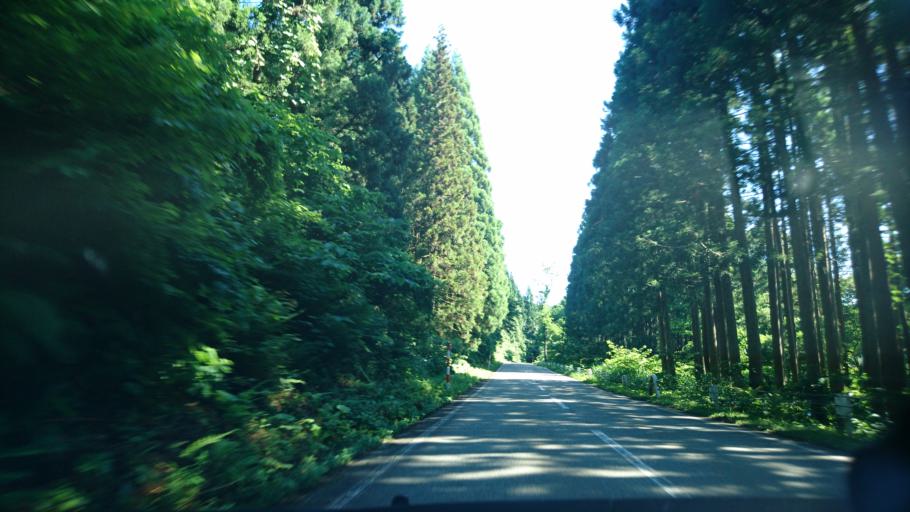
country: JP
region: Akita
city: Kakunodatemachi
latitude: 39.7441
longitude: 140.6368
